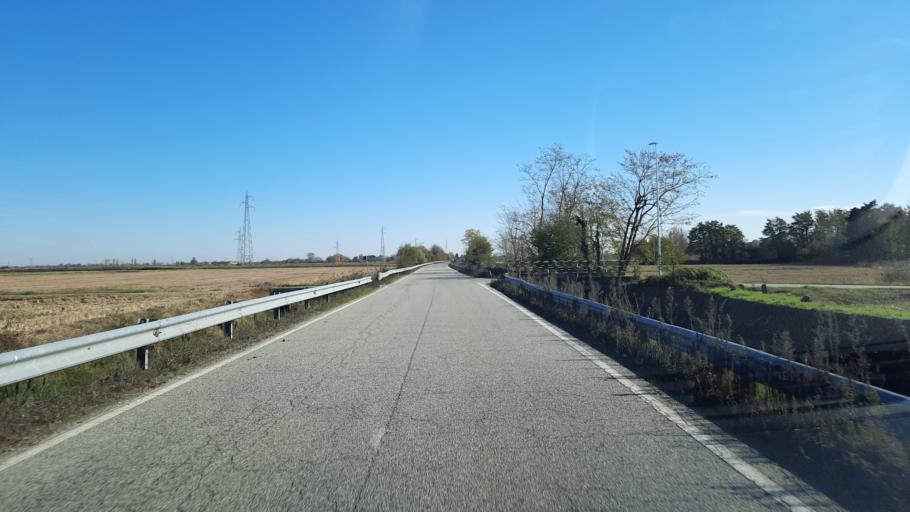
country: IT
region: Piedmont
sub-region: Provincia di Alessandria
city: Balzola
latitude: 45.1879
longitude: 8.4093
